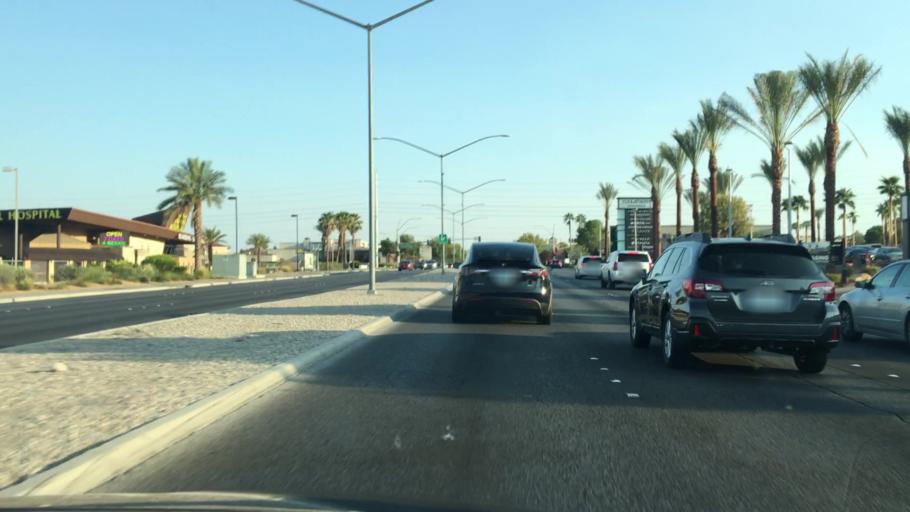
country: US
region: Nevada
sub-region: Clark County
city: Summerlin South
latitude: 36.1610
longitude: -115.2915
